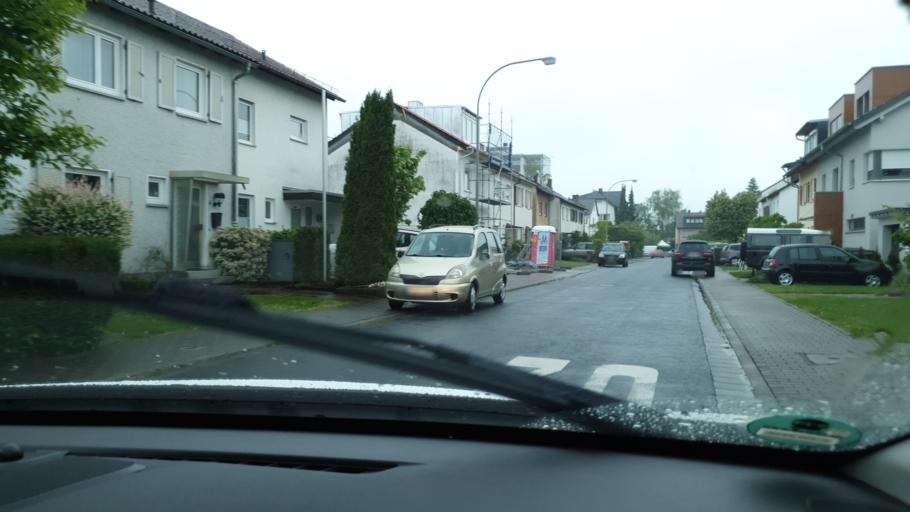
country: DE
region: Hesse
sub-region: Regierungsbezirk Darmstadt
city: Oberursel
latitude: 50.2049
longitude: 8.5826
